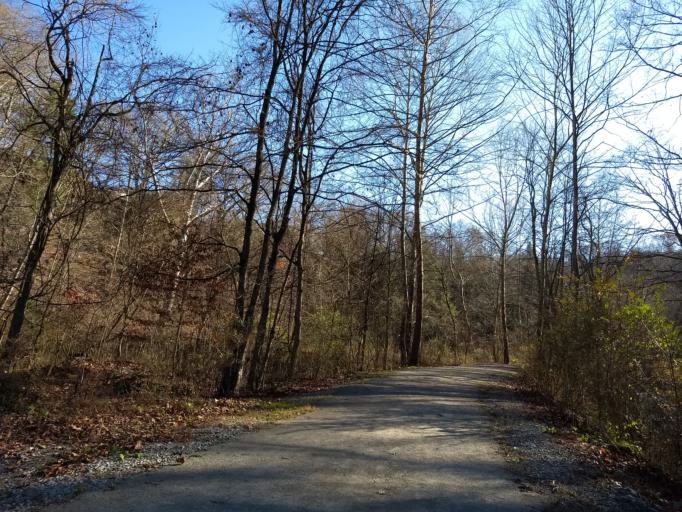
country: US
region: Pennsylvania
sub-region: Allegheny County
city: South Park Township
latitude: 40.2798
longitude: -79.9815
